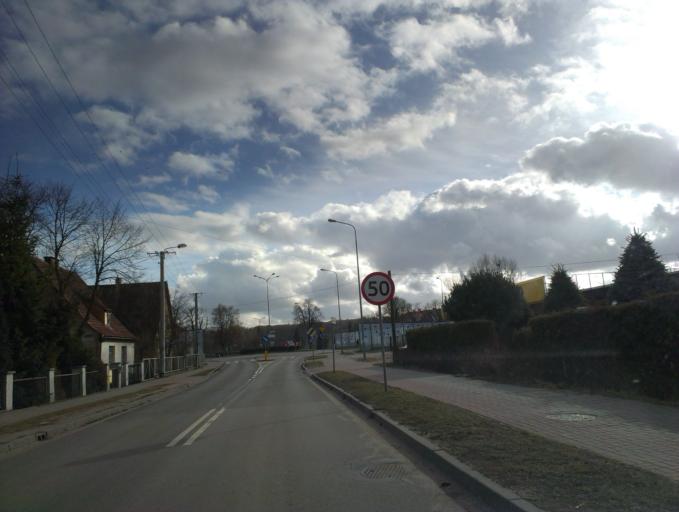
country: PL
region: Pomeranian Voivodeship
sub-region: Powiat czluchowski
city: Czluchow
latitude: 53.6741
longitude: 17.3675
